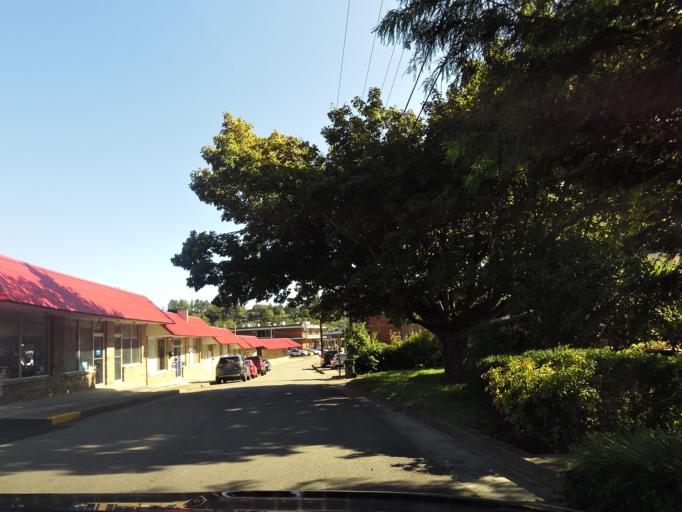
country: US
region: Kentucky
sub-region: Whitley County
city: Williamsburg
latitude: 36.7421
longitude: -84.1620
